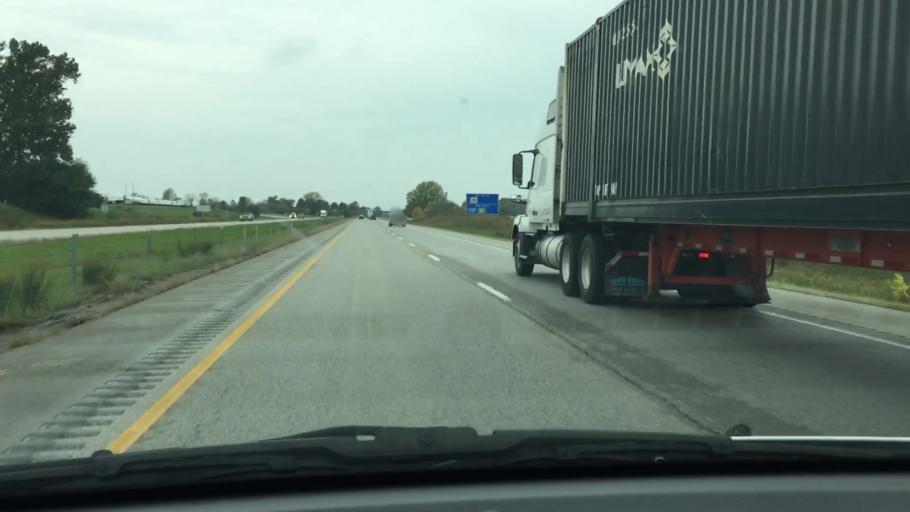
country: US
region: Iowa
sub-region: Johnson County
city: Tiffin
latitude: 41.6942
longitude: -91.6548
